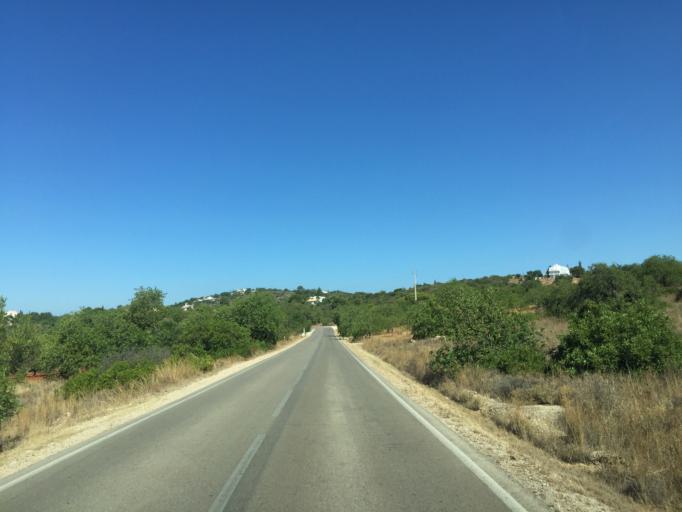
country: PT
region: Faro
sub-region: Loule
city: Vilamoura
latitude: 37.1142
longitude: -8.0757
